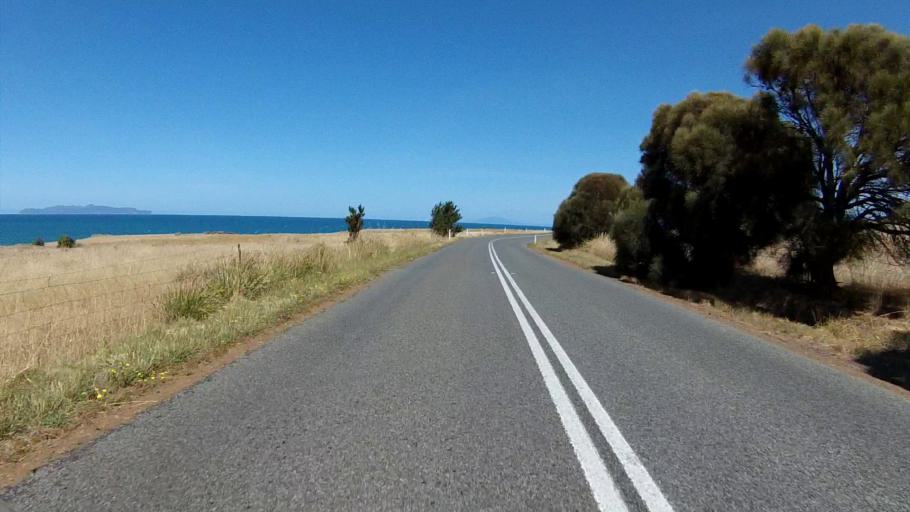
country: AU
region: Tasmania
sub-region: Sorell
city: Sorell
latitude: -42.1705
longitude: 148.0738
